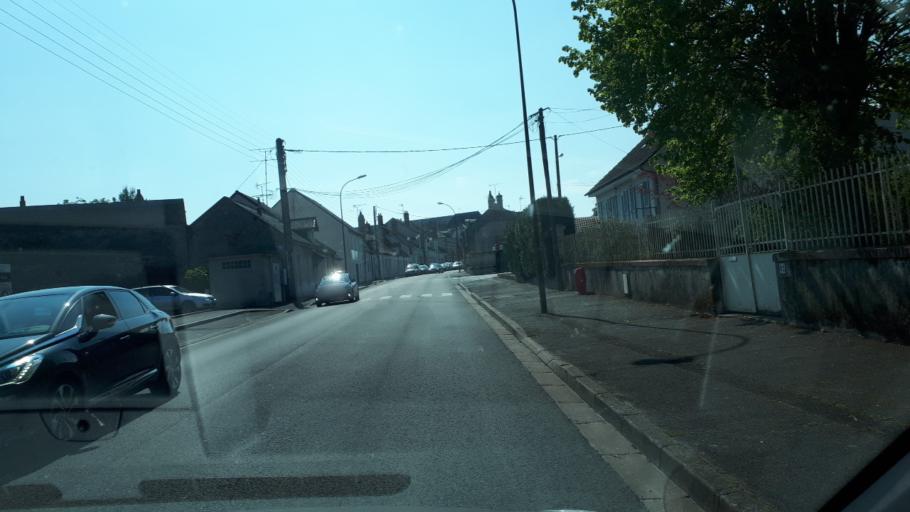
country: FR
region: Centre
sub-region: Departement du Loir-et-Cher
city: Romorantin-Lanthenay
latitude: 47.3655
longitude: 1.7409
